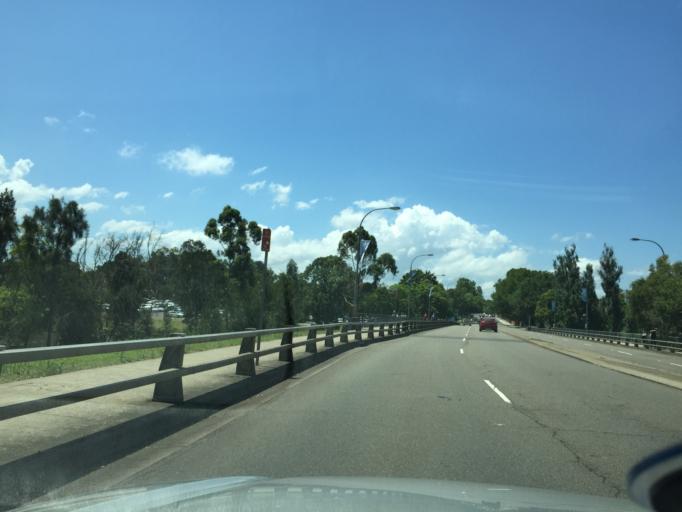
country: AU
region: New South Wales
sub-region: Parramatta
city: City of Parramatta
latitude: -33.8120
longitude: 151.0004
